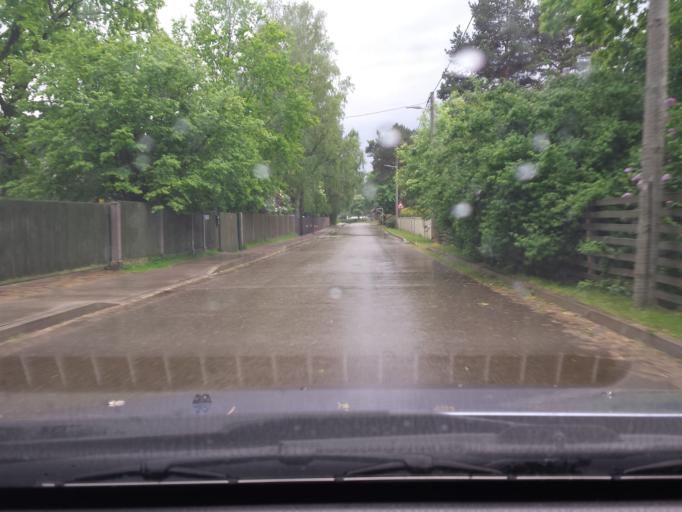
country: LV
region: Riga
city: Bolderaja
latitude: 57.0743
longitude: 24.0958
